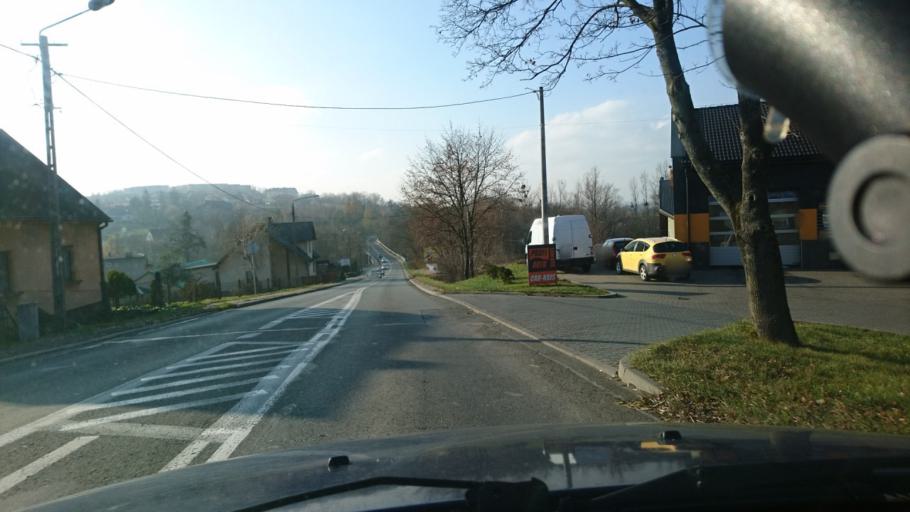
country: PL
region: Silesian Voivodeship
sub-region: Powiat cieszynski
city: Zamarski
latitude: 49.7518
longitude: 18.6644
